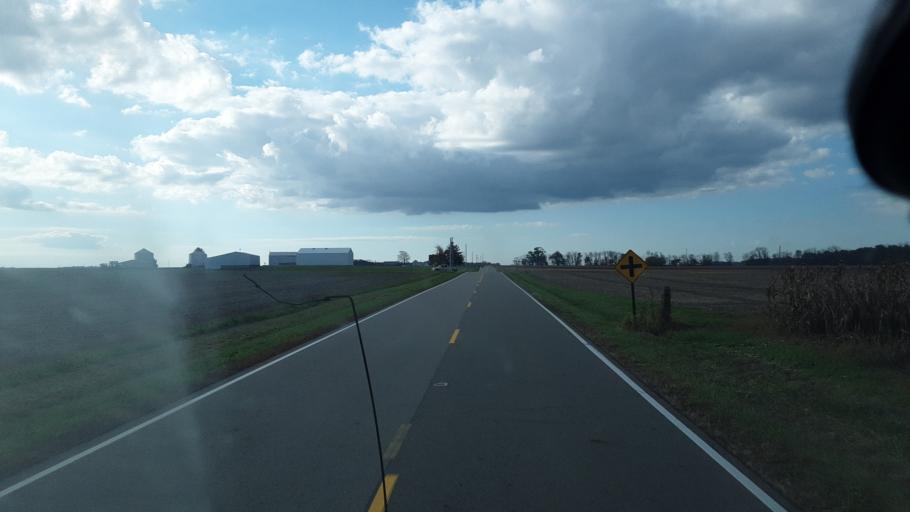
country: US
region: Ohio
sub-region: Fayette County
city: Washington Court House
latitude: 39.4423
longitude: -83.4381
